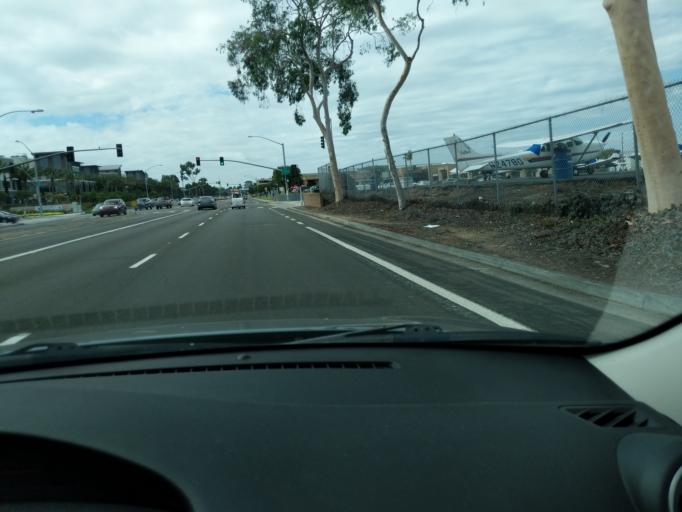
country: US
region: California
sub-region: San Diego County
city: San Diego
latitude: 32.8098
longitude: -117.1393
